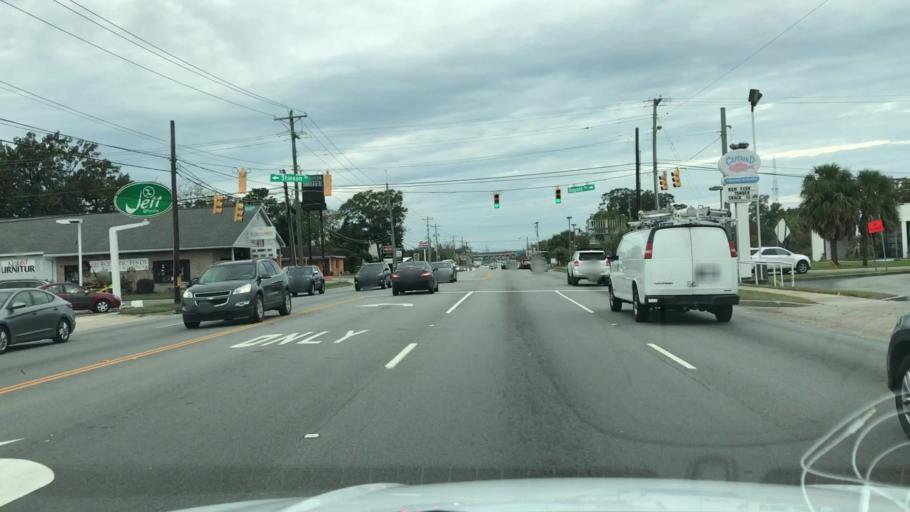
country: US
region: South Carolina
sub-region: Charleston County
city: Shell Point
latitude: 32.7888
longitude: -80.0245
